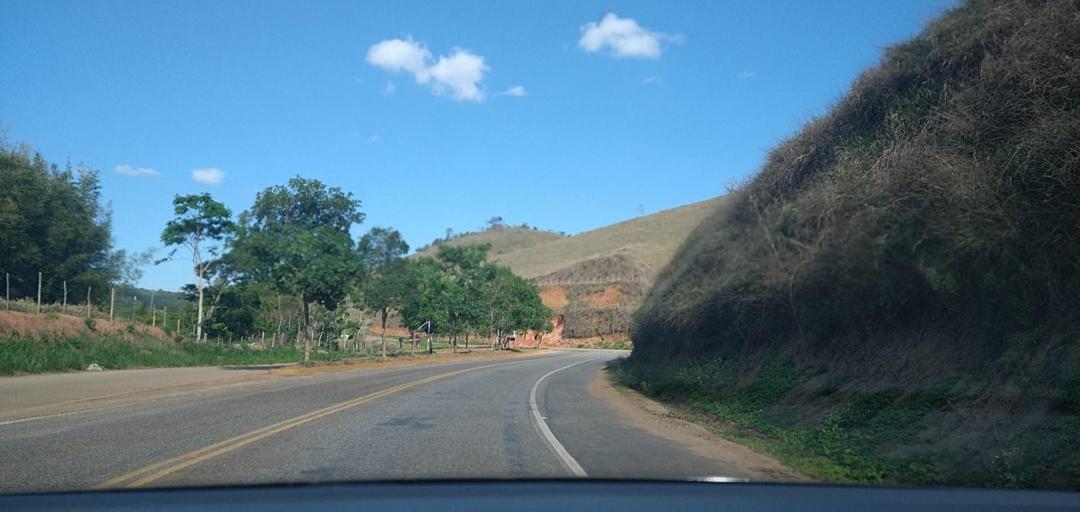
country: BR
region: Minas Gerais
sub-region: Alvinopolis
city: Alvinopolis
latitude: -20.1679
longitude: -42.9246
